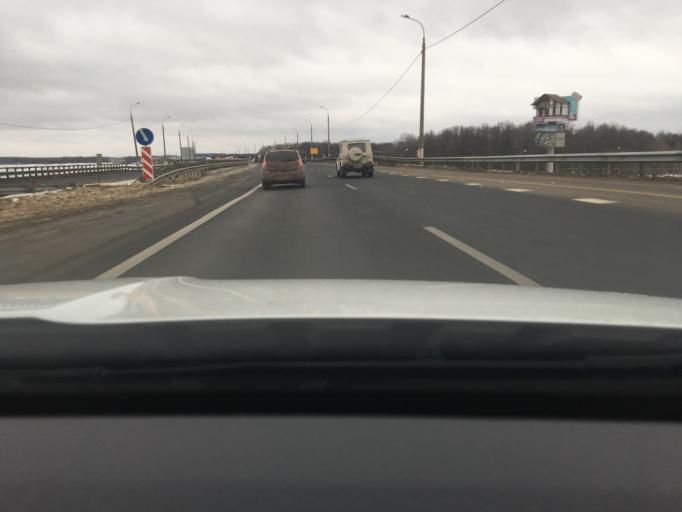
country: RU
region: Moskovskaya
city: Serpukhov
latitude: 54.8340
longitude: 37.4619
